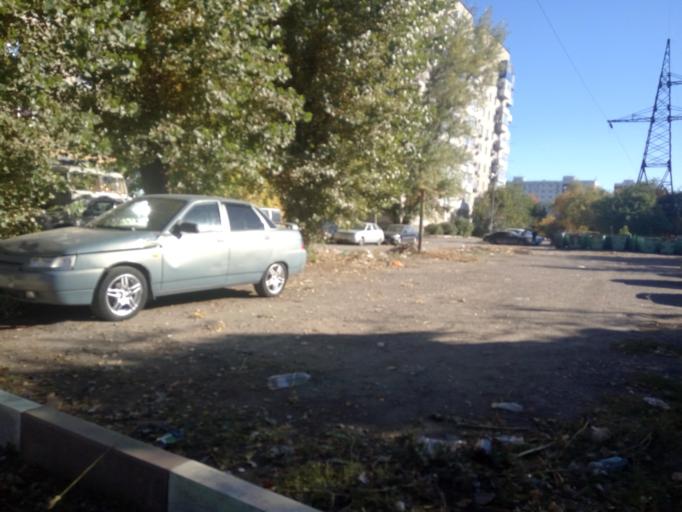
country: RU
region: Rostov
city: Bataysk
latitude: 47.1231
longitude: 39.7326
